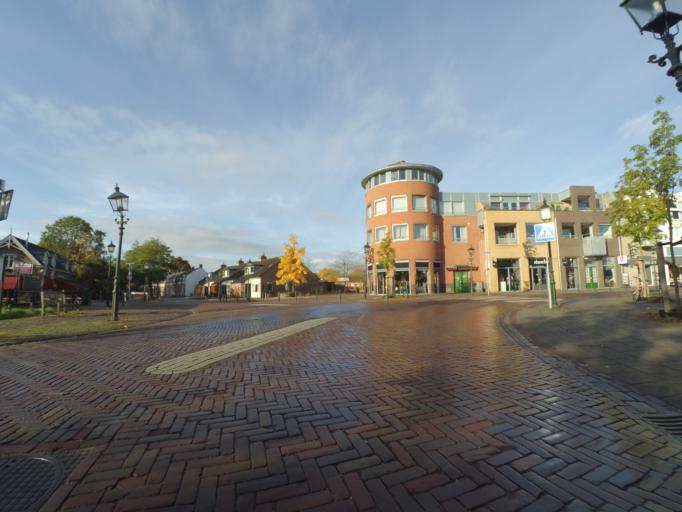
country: NL
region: Utrecht
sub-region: Gemeente Wijk bij Duurstede
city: Wijk bij Duurstede
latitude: 51.9742
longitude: 5.3448
